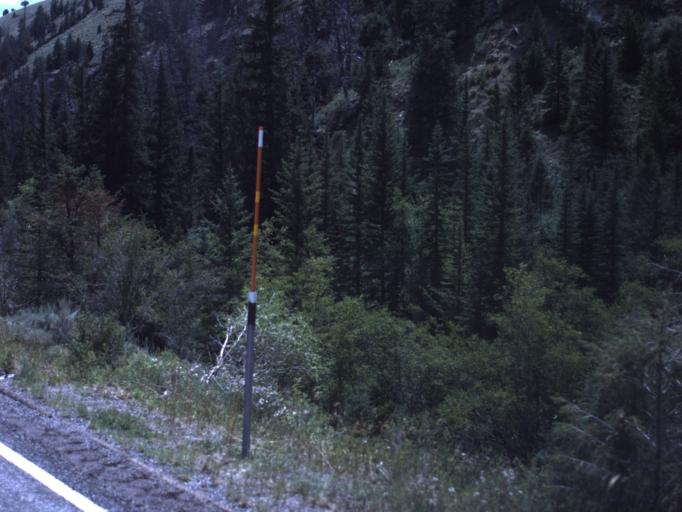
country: US
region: Utah
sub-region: Emery County
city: Huntington
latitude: 39.4711
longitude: -111.1546
